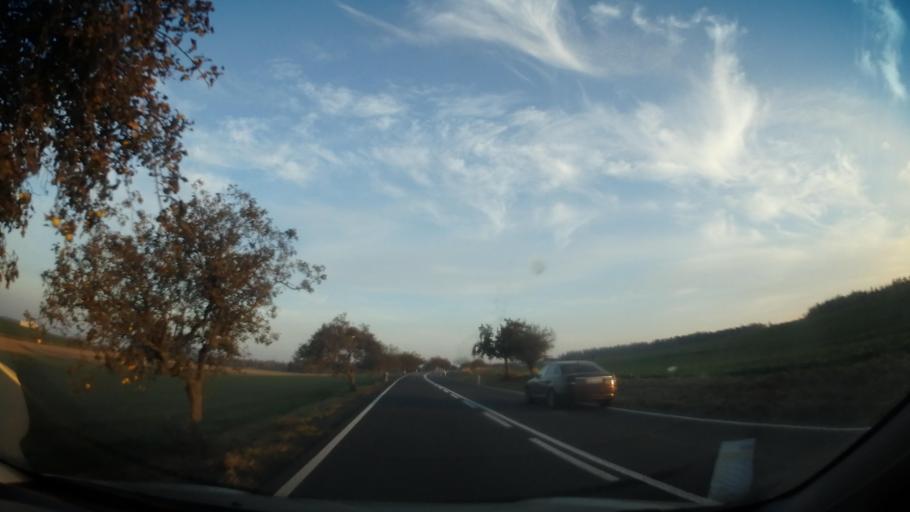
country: CZ
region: Central Bohemia
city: Vlasim
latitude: 49.6848
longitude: 14.9419
